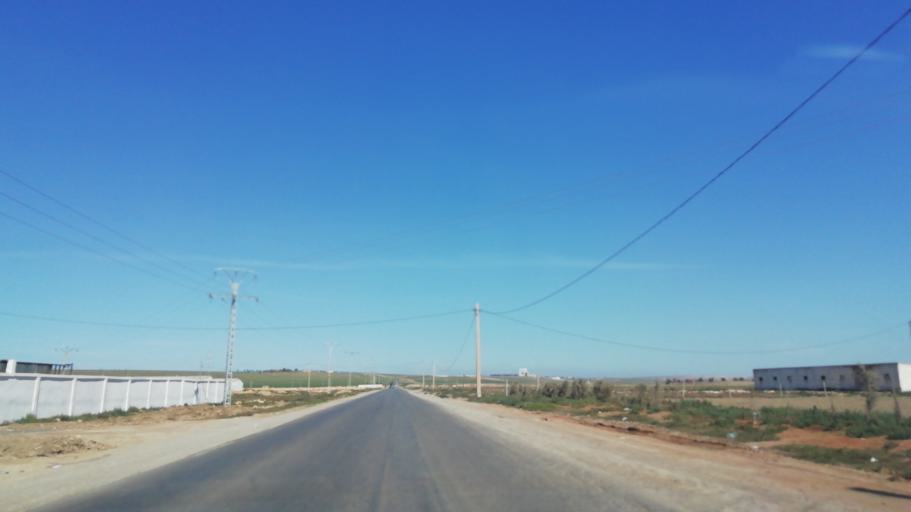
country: DZ
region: Oran
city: Es Senia
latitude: 35.5221
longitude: -0.5879
